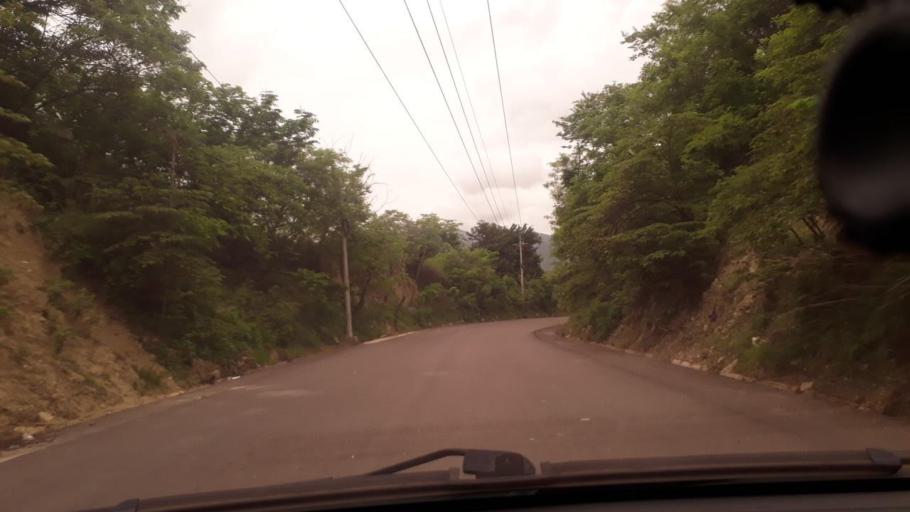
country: GT
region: Chiquimula
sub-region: Municipio de San Juan Ermita
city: San Juan Ermita
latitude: 14.7351
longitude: -89.4817
